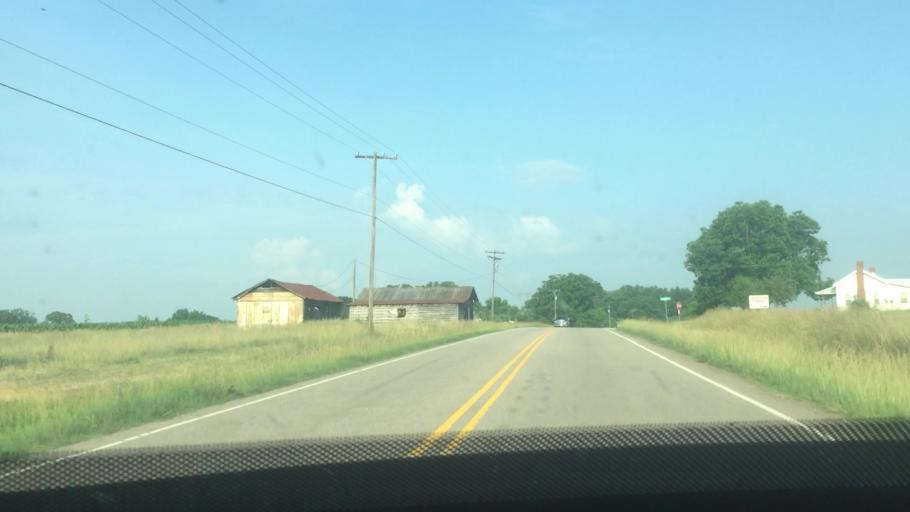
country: US
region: North Carolina
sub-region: Rowan County
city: Enochville
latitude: 35.5816
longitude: -80.7265
